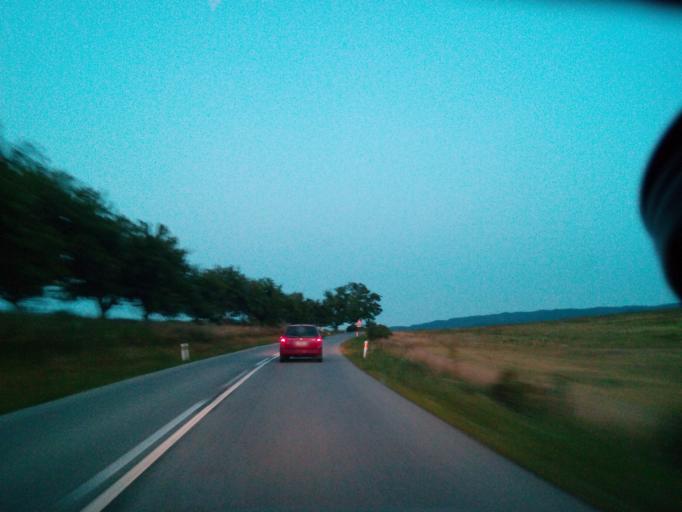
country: SK
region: Presovsky
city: Spisske Podhradie
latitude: 48.9441
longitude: 20.7168
